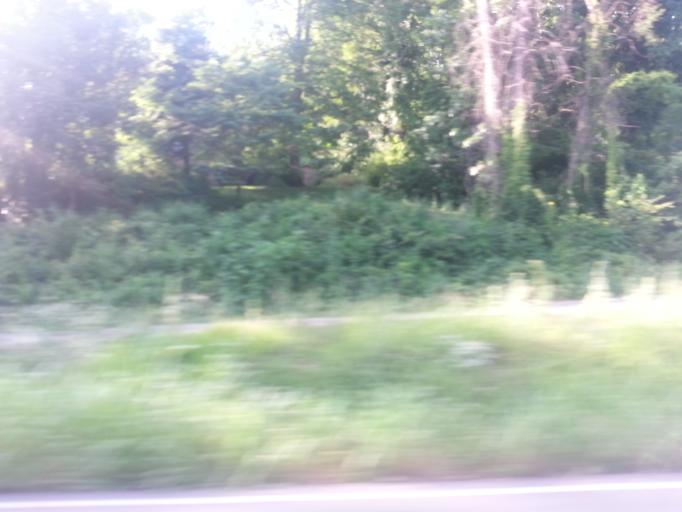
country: US
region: Tennessee
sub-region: Knox County
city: Knoxville
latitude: 35.9207
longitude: -83.9448
